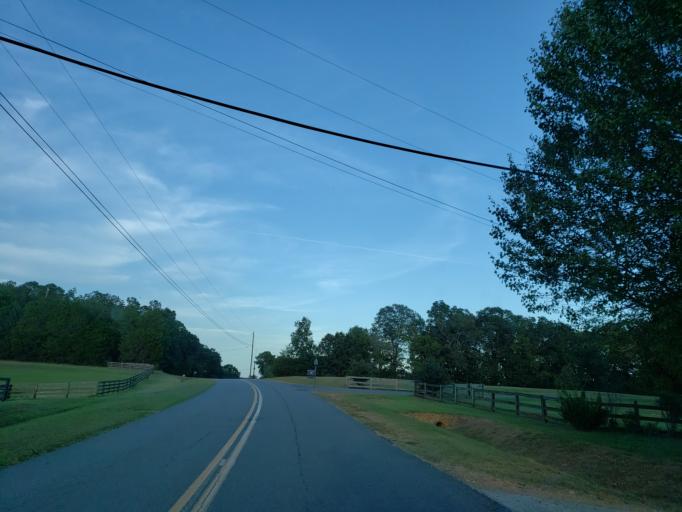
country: US
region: Georgia
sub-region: Floyd County
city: Rome
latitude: 34.2419
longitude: -85.1242
